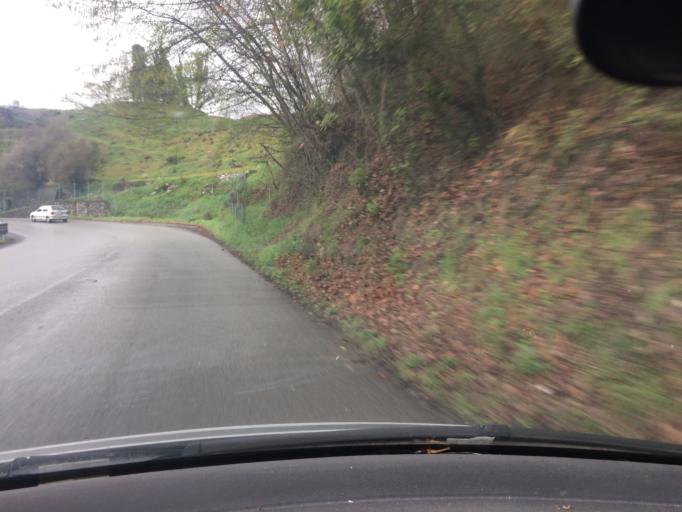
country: IT
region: Tuscany
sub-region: Provincia di Massa-Carrara
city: Massa
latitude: 44.0653
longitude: 10.1133
